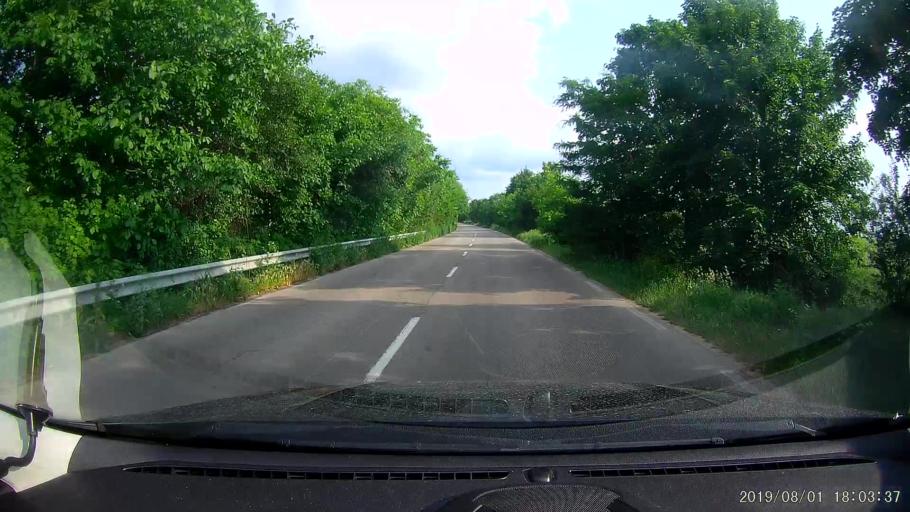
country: BG
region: Silistra
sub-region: Obshtina Alfatar
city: Alfatar
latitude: 43.9233
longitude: 27.2889
